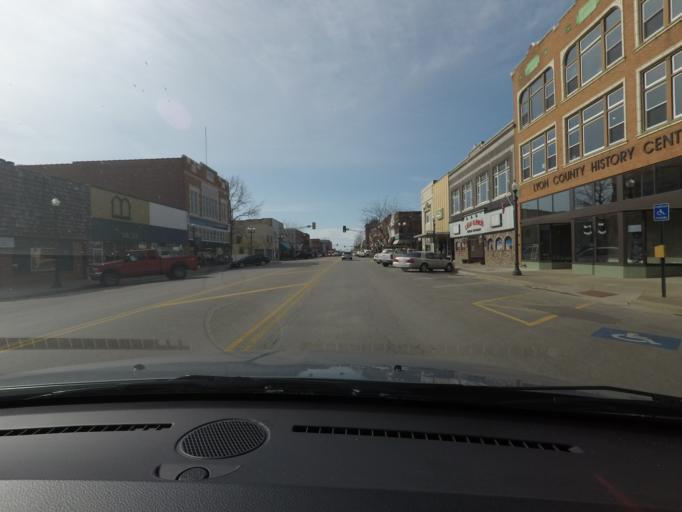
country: US
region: Kansas
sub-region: Lyon County
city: Emporia
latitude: 38.4068
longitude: -96.1802
